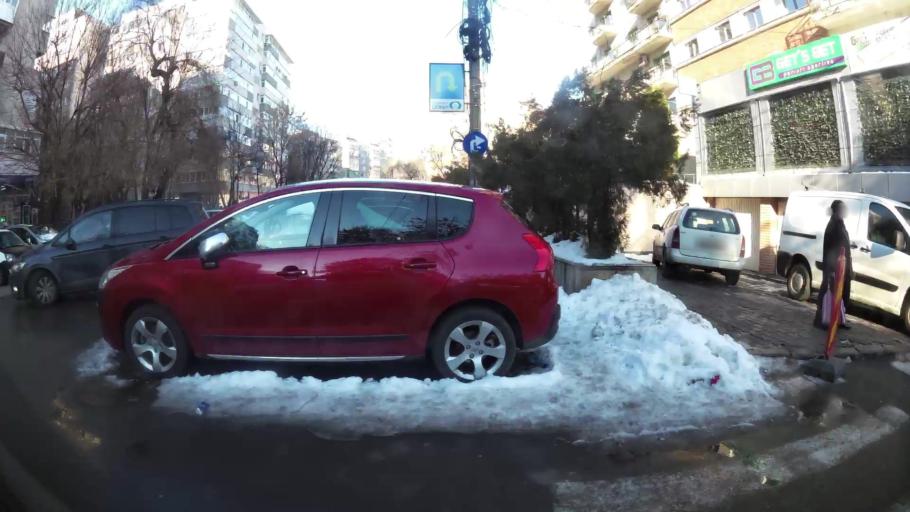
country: RO
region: Bucuresti
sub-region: Municipiul Bucuresti
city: Bucharest
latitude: 44.4139
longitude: 26.1089
